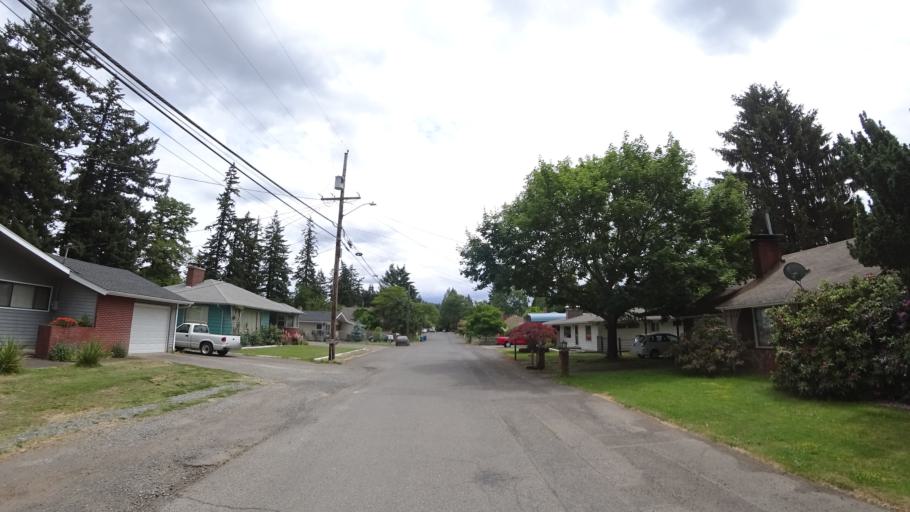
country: US
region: Oregon
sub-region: Multnomah County
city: Lents
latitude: 45.4860
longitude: -122.5364
